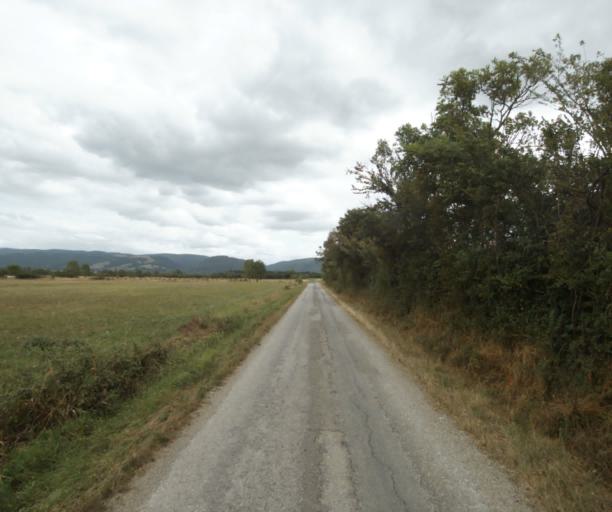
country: FR
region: Midi-Pyrenees
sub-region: Departement de la Haute-Garonne
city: Revel
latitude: 43.4777
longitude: 2.0329
